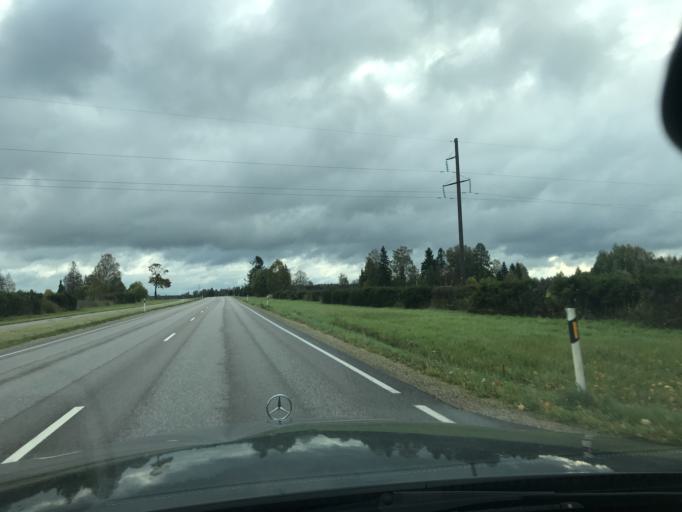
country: EE
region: Valgamaa
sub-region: Torva linn
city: Torva
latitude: 58.0111
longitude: 25.8934
